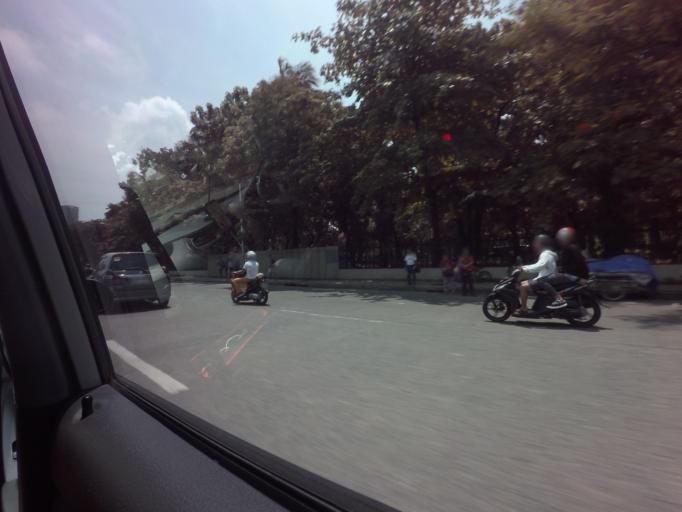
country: PH
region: Metro Manila
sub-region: City of Manila
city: Quiapo
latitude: 14.5918
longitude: 120.9804
